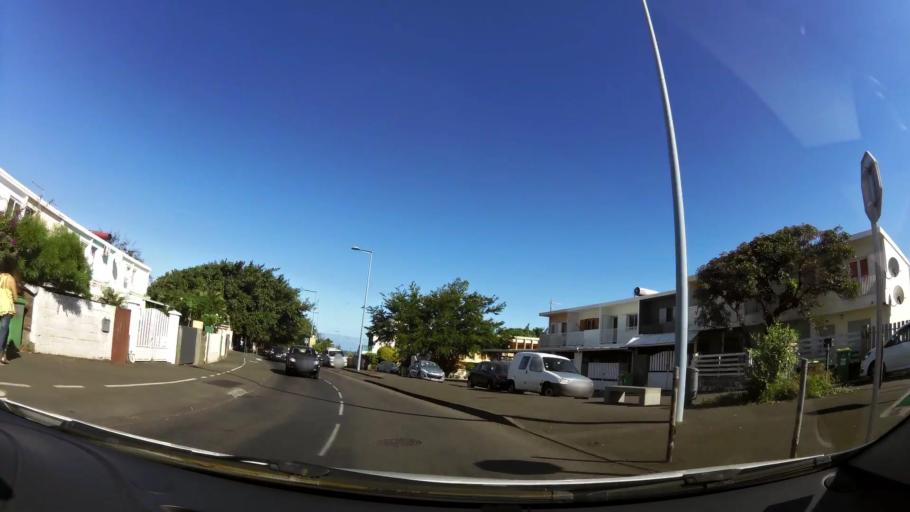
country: RE
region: Reunion
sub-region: Reunion
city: Saint-Pierre
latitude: -21.3433
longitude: 55.4867
